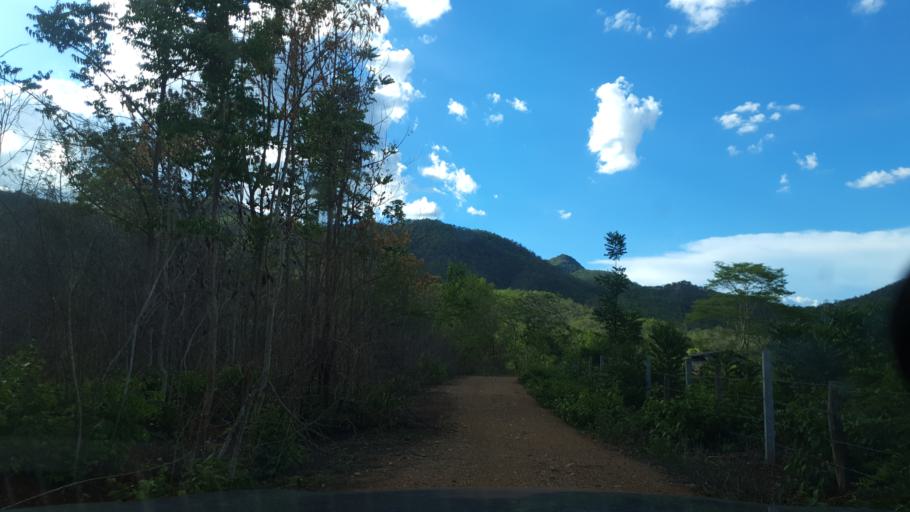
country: TH
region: Lampang
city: Sop Prap
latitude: 17.8513
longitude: 99.2843
